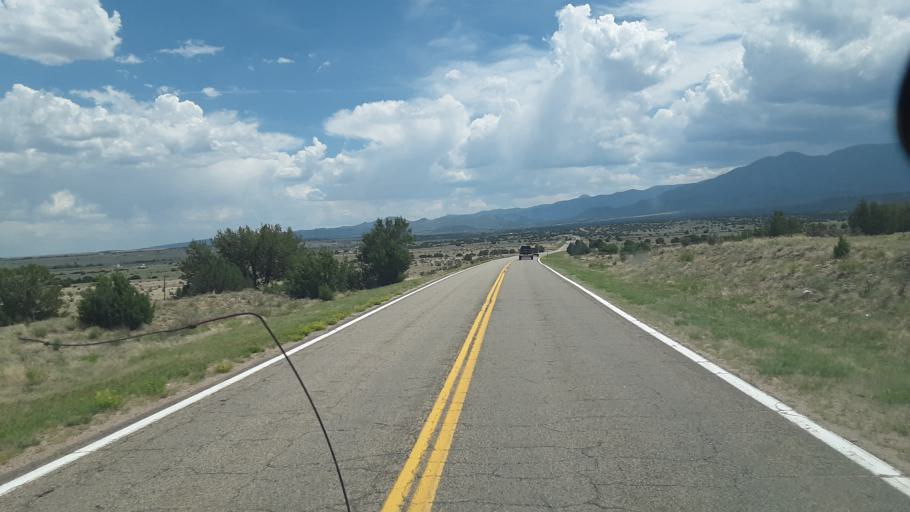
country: US
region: Colorado
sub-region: Fremont County
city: Florence
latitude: 38.3261
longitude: -105.1053
